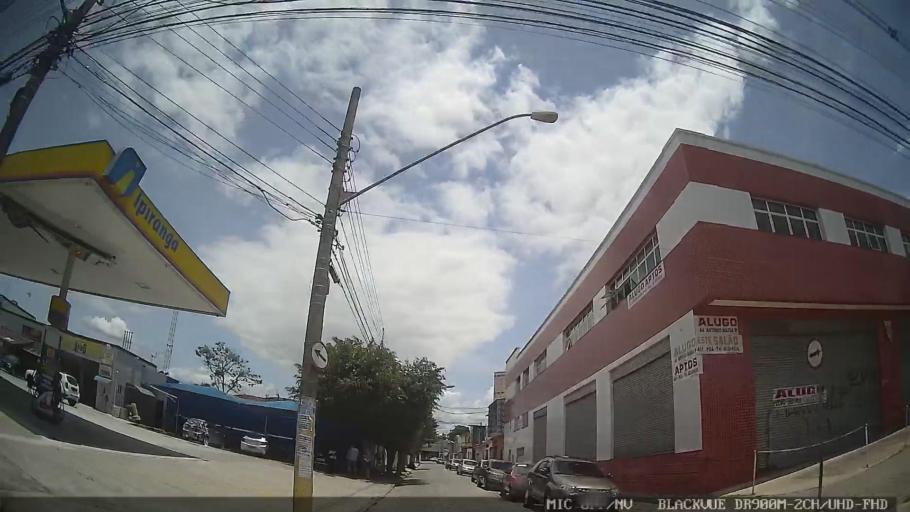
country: BR
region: Sao Paulo
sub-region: Poa
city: Poa
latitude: -23.5239
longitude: -46.3379
